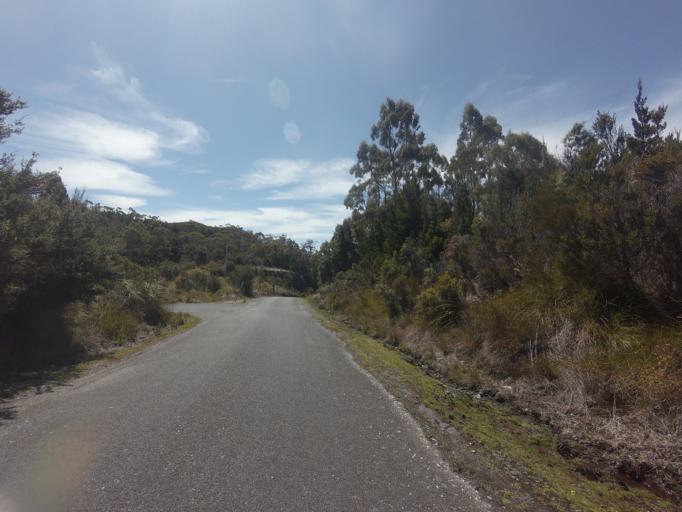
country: AU
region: Tasmania
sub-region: West Coast
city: Queenstown
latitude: -42.7828
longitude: 146.0324
